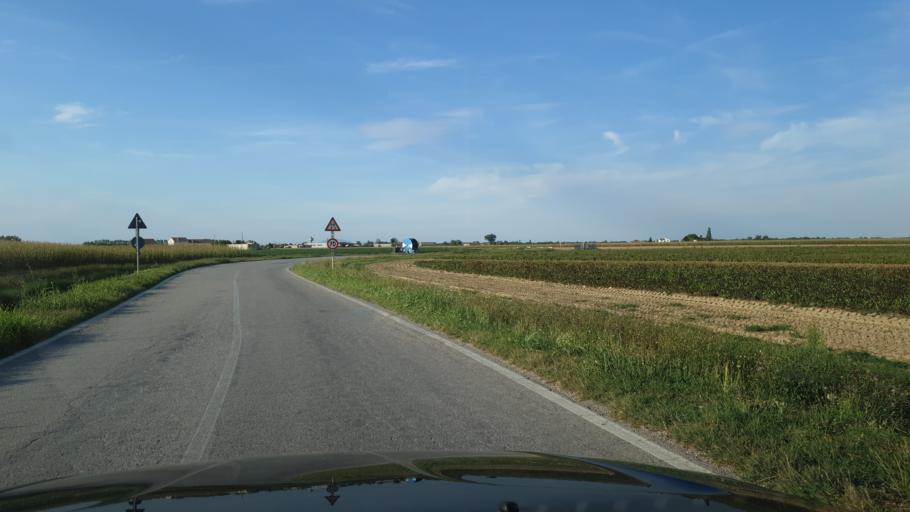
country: IT
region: Veneto
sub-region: Provincia di Rovigo
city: Fiesso Umbertiano
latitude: 44.9762
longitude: 11.6083
